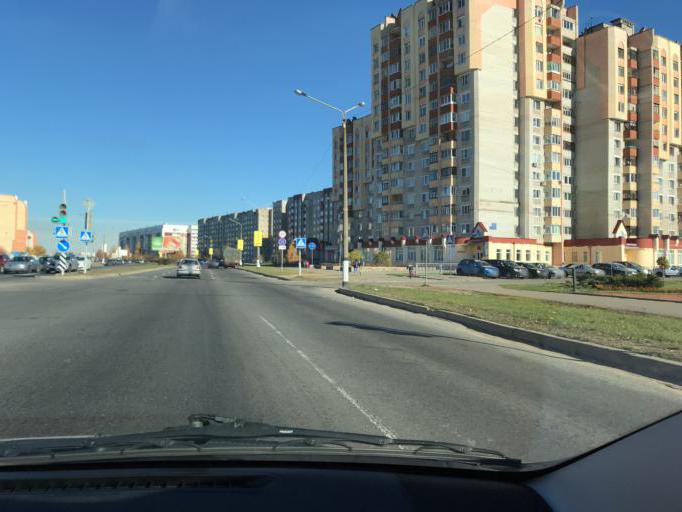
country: BY
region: Vitebsk
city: Polatsk
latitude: 55.4926
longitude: 28.7513
